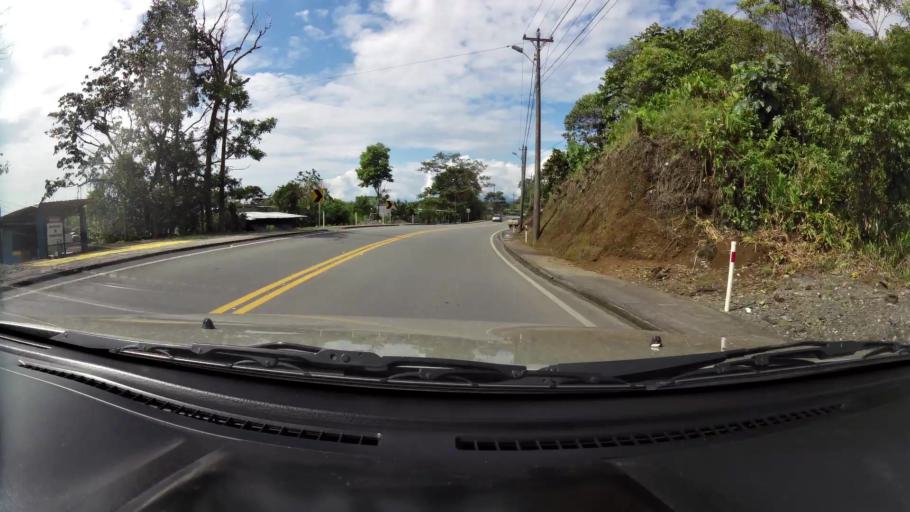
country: EC
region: Pastaza
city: Puyo
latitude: -1.4973
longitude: -78.0217
